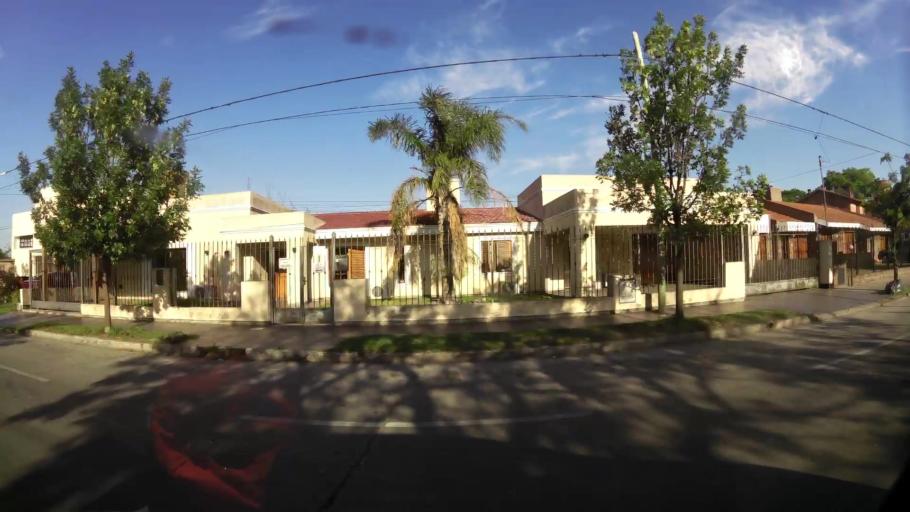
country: AR
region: Cordoba
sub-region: Departamento de Capital
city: Cordoba
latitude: -31.3694
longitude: -64.2264
